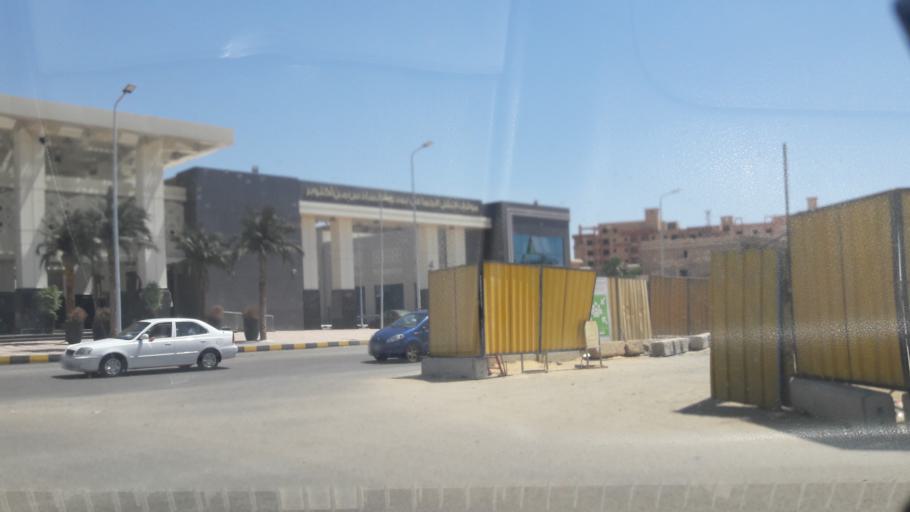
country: EG
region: Al Jizah
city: Madinat Sittah Uktubar
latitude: 29.9691
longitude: 30.9330
